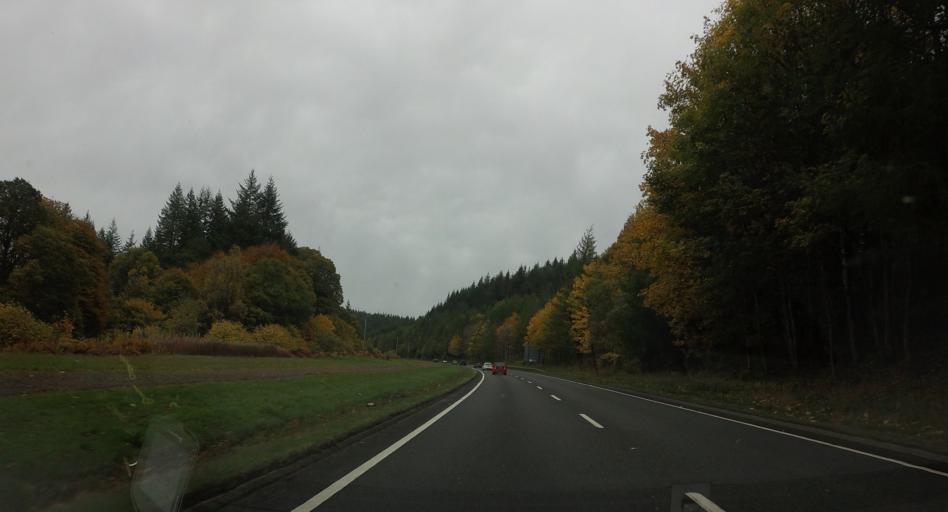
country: GB
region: Scotland
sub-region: Perth and Kinross
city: Bankfoot
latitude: 56.5677
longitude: -3.6233
